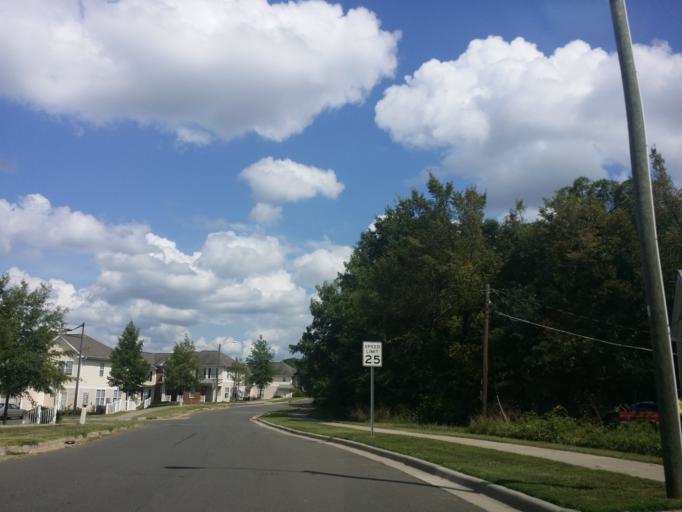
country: US
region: North Carolina
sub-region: Durham County
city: Durham
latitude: 35.9859
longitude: -78.8921
